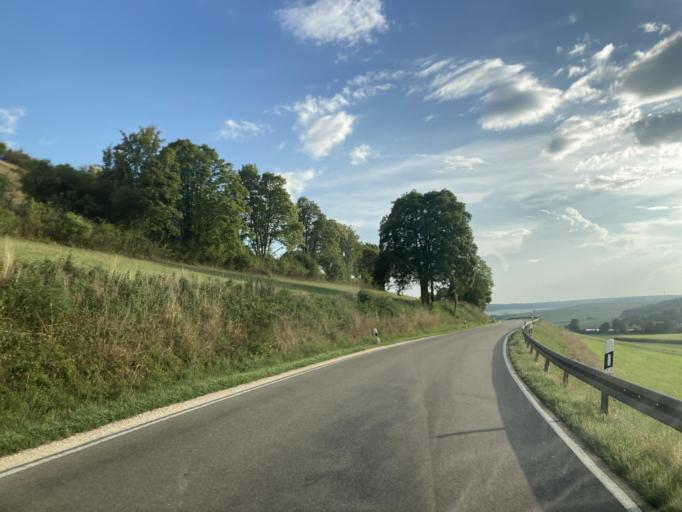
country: DE
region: Baden-Wuerttemberg
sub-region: Regierungsbezirk Stuttgart
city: Dischingen
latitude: 48.7207
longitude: 10.3856
